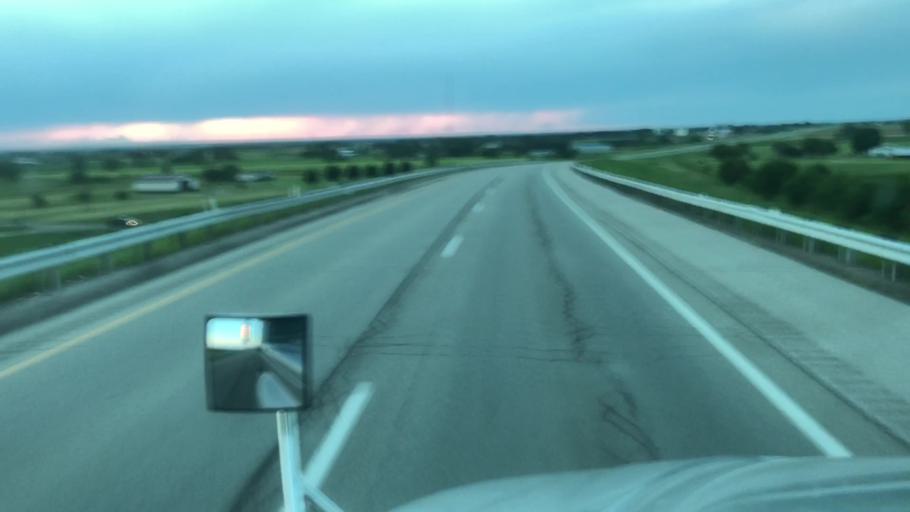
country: US
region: Oklahoma
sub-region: Kay County
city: Ponca City
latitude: 36.7749
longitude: -97.0660
